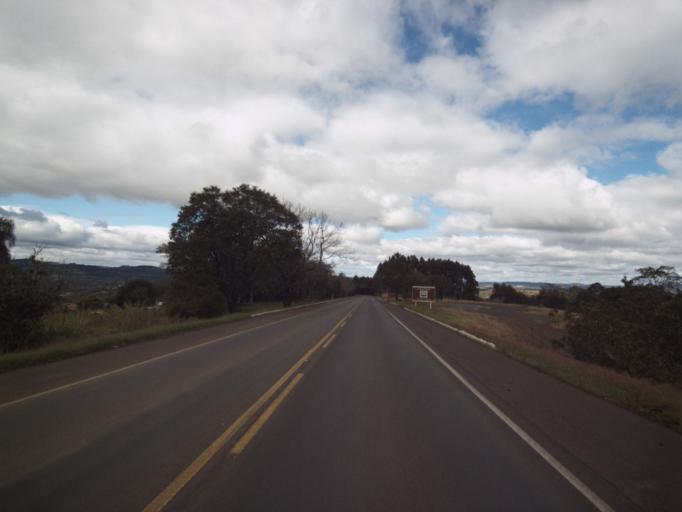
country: BR
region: Santa Catarina
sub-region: Concordia
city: Concordia
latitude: -27.3223
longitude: -51.9817
